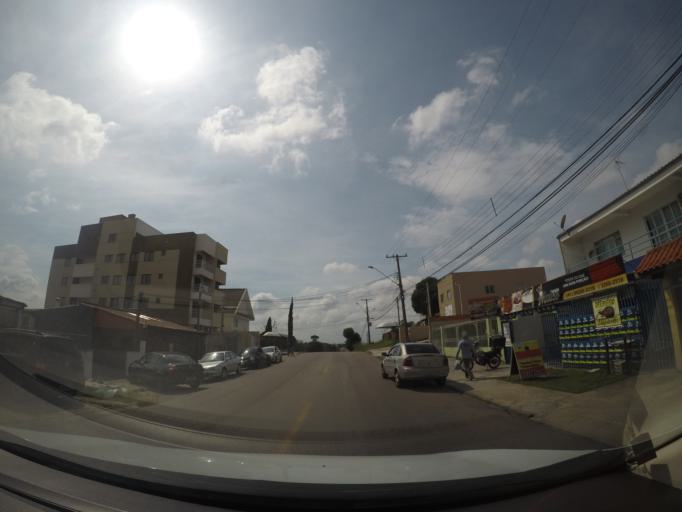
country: BR
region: Parana
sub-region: Curitiba
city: Curitiba
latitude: -25.4899
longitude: -49.2864
